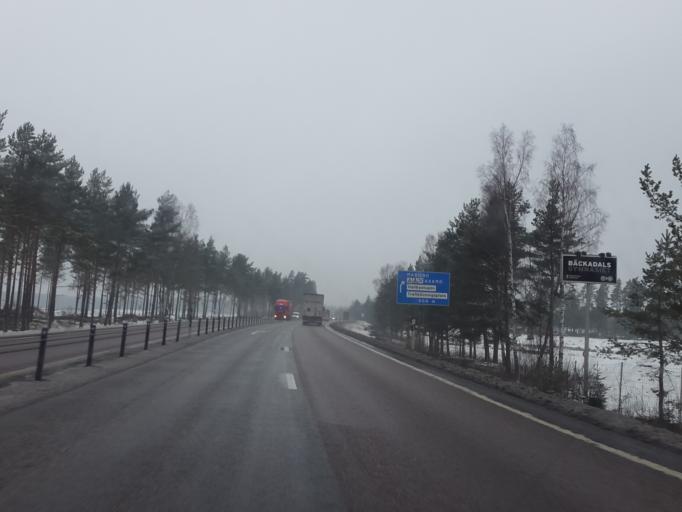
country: SE
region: Joenkoeping
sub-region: Jonkopings Kommun
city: Jonkoping
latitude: 57.7681
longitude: 14.0899
